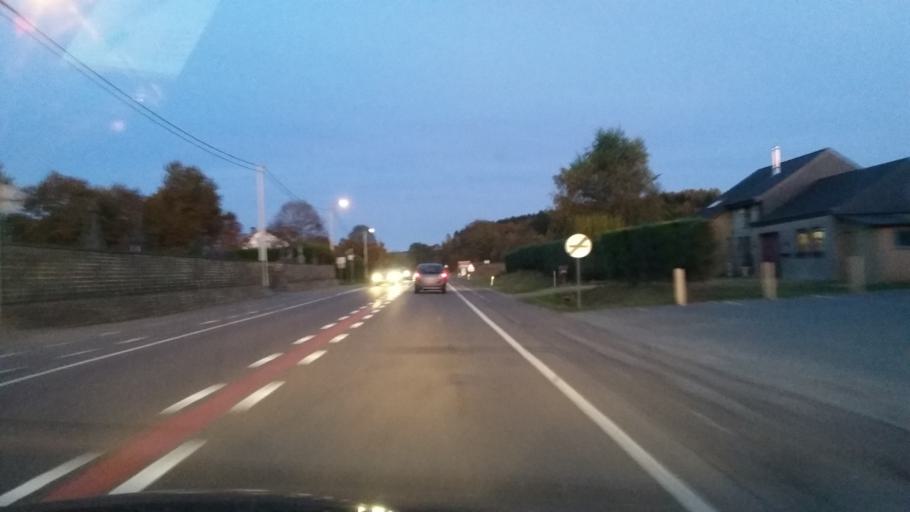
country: BE
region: Wallonia
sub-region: Province du Luxembourg
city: Saint-Leger
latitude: 49.6692
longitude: 5.6744
